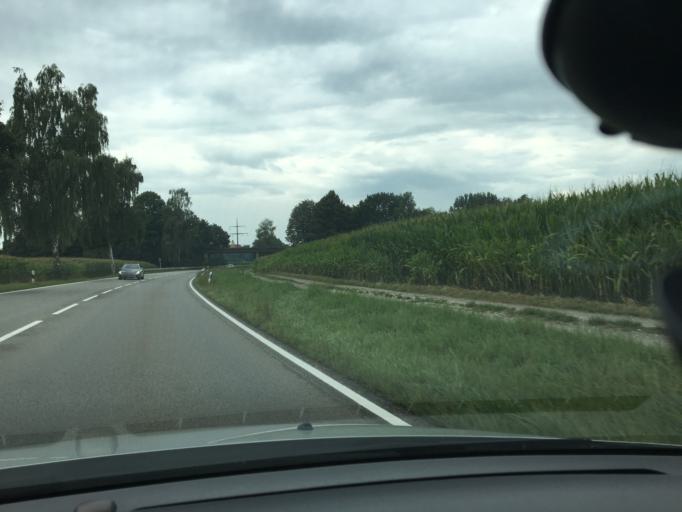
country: DE
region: Bavaria
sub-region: Upper Bavaria
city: Muehldorf
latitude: 48.2418
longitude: 12.4986
